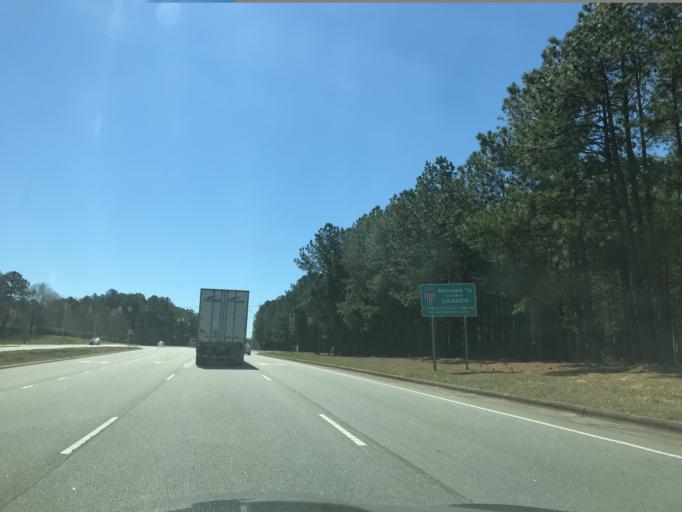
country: US
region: North Carolina
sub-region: Wake County
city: Garner
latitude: 35.7261
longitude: -78.6401
